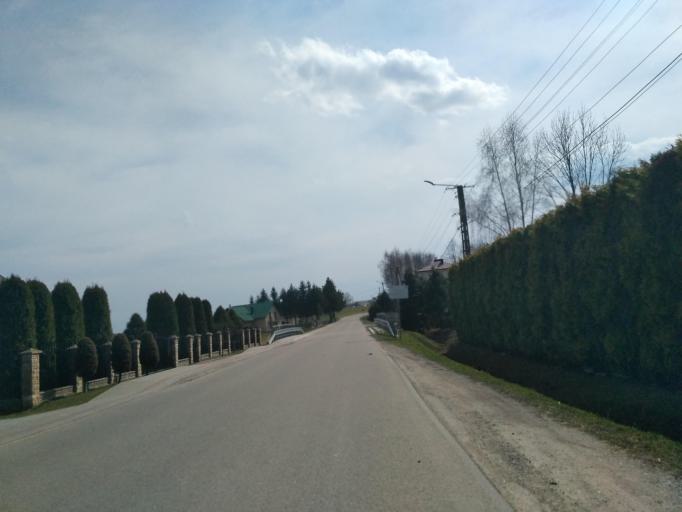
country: PL
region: Subcarpathian Voivodeship
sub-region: Powiat ropczycko-sedziszowski
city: Iwierzyce
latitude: 50.0265
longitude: 21.7666
